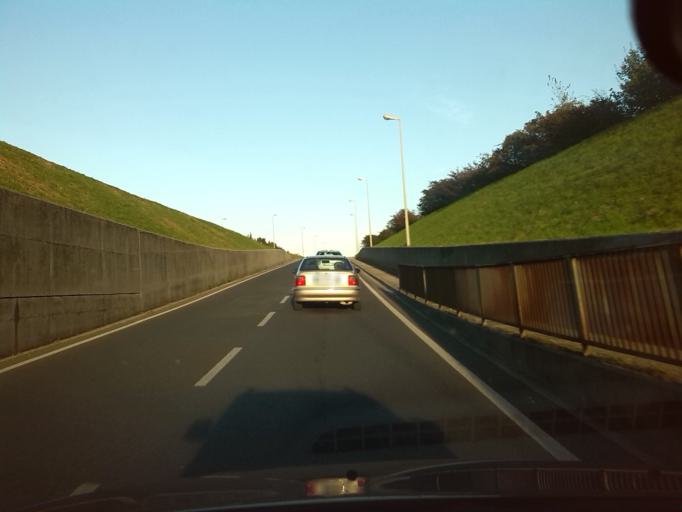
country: IT
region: Friuli Venezia Giulia
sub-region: Provincia di Udine
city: Basaldella
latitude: 46.0296
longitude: 13.2391
